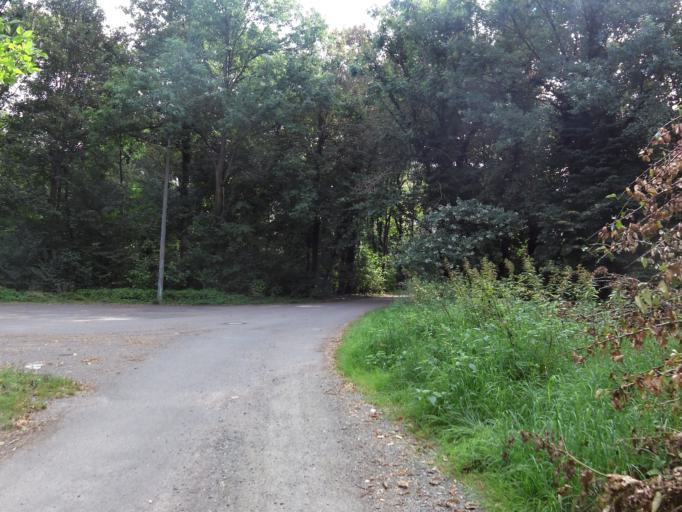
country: DE
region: Saxony
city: Schkeuditz
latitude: 51.3628
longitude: 12.2922
